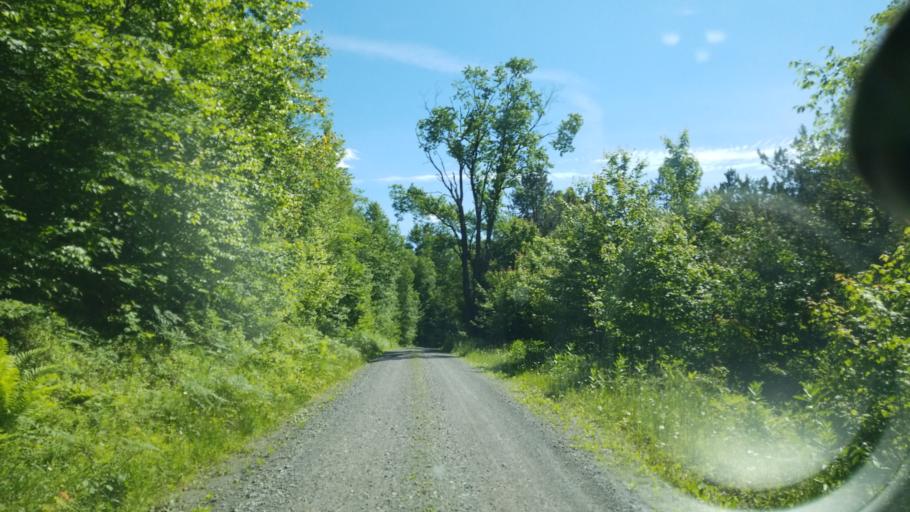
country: US
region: Pennsylvania
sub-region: Clearfield County
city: Clearfield
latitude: 41.2107
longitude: -78.3871
